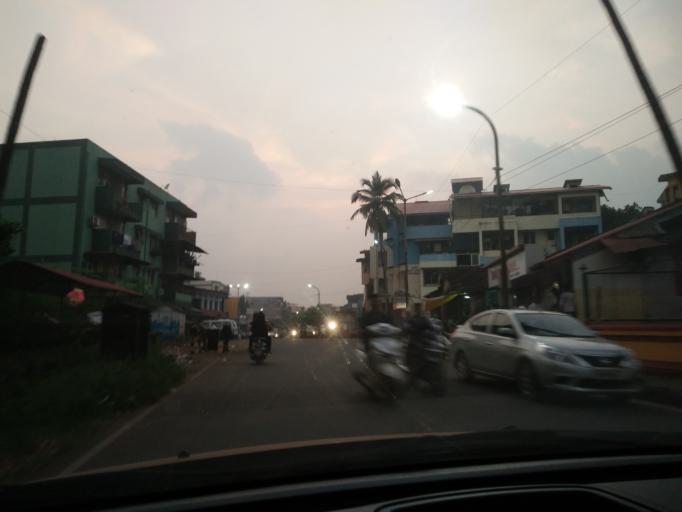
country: IN
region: Goa
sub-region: South Goa
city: Madgaon
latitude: 15.2725
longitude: 73.9716
